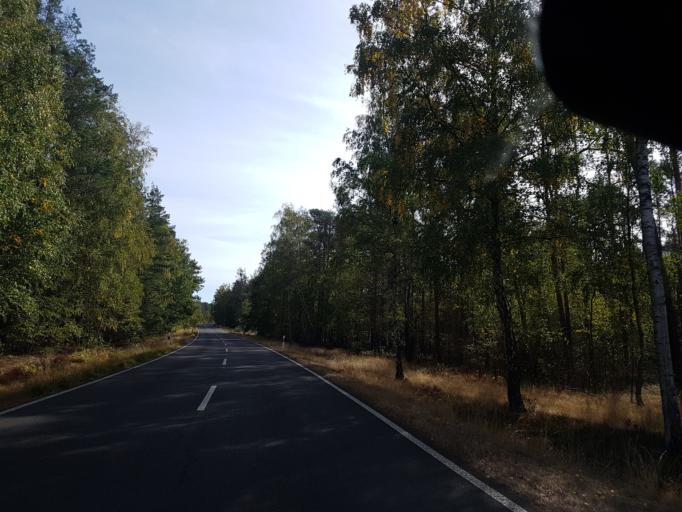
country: DE
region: Brandenburg
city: Schlieben
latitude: 51.6840
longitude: 13.4550
